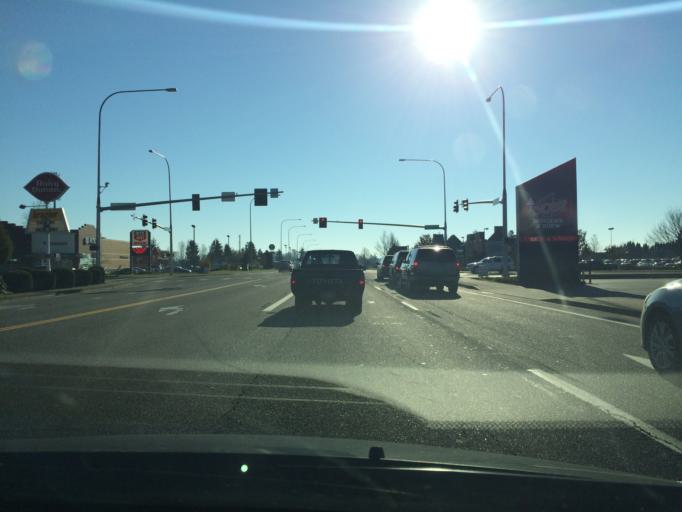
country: US
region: Washington
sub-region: Whatcom County
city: Lynden
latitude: 48.9357
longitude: -122.4855
